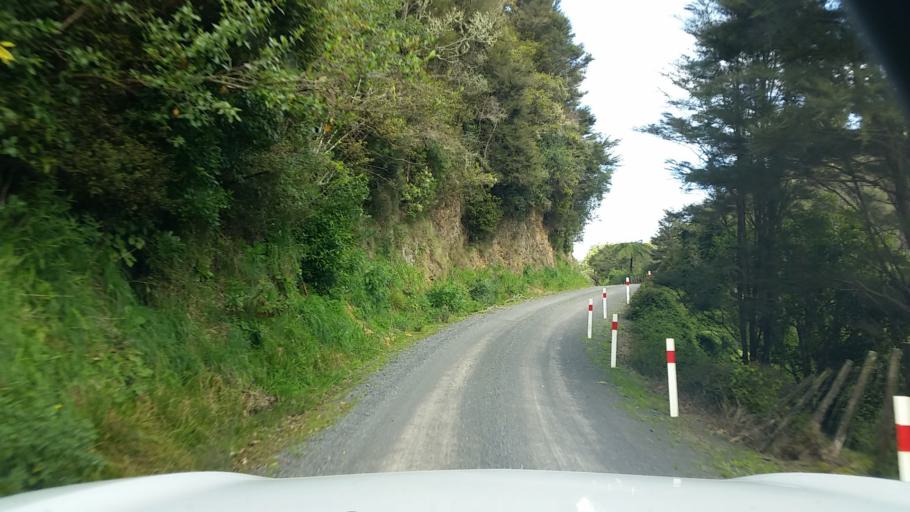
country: NZ
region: Waikato
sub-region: Hauraki District
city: Ngatea
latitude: -37.4714
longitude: 175.4572
